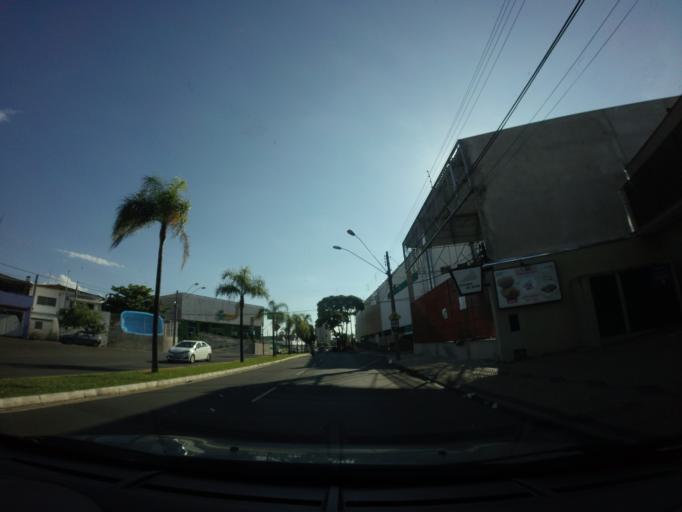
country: BR
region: Sao Paulo
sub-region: Rio Claro
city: Rio Claro
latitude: -22.4125
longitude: -47.5690
